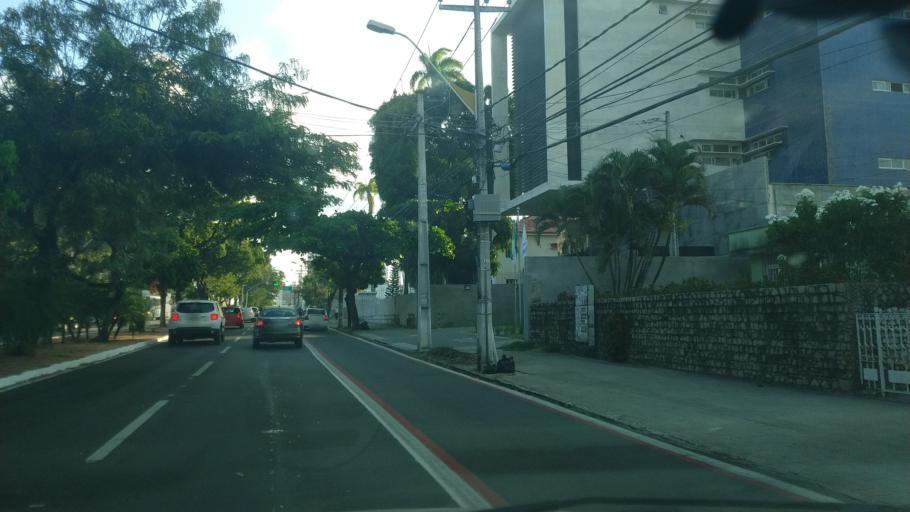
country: BR
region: Rio Grande do Norte
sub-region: Natal
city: Natal
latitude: -5.7915
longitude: -35.1974
